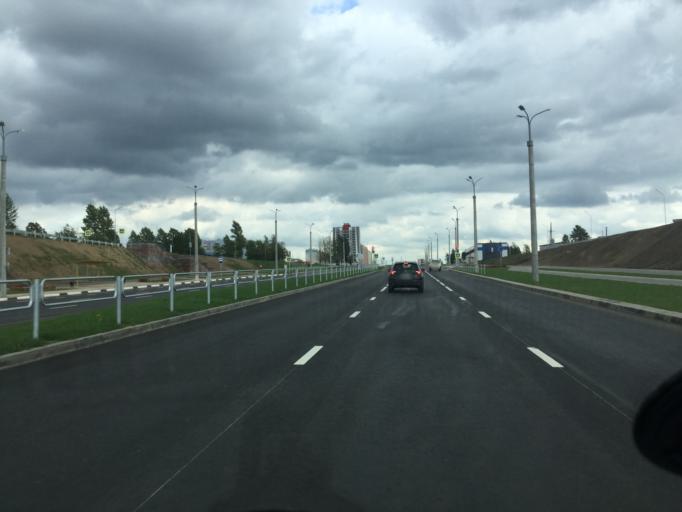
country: BY
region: Vitebsk
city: Vitebsk
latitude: 55.1674
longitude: 30.2472
